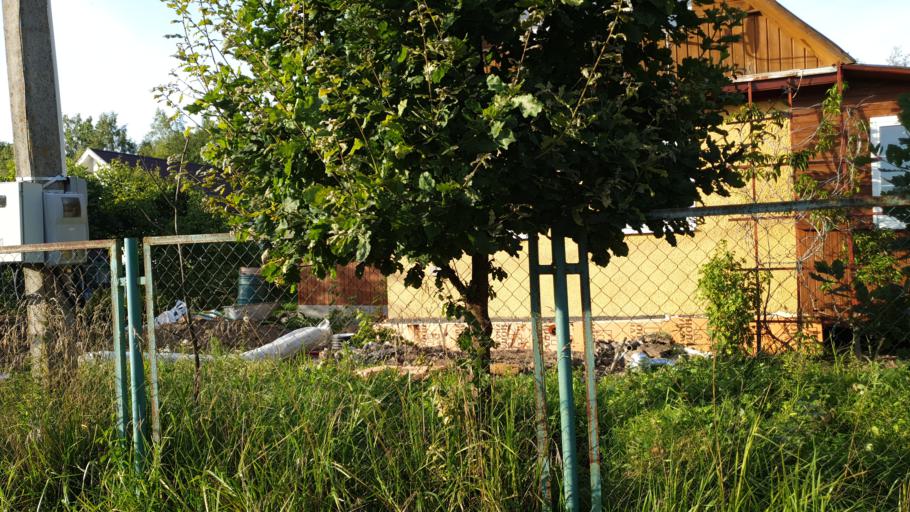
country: RU
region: Leningrad
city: Ivangorod
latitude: 59.4225
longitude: 28.3370
